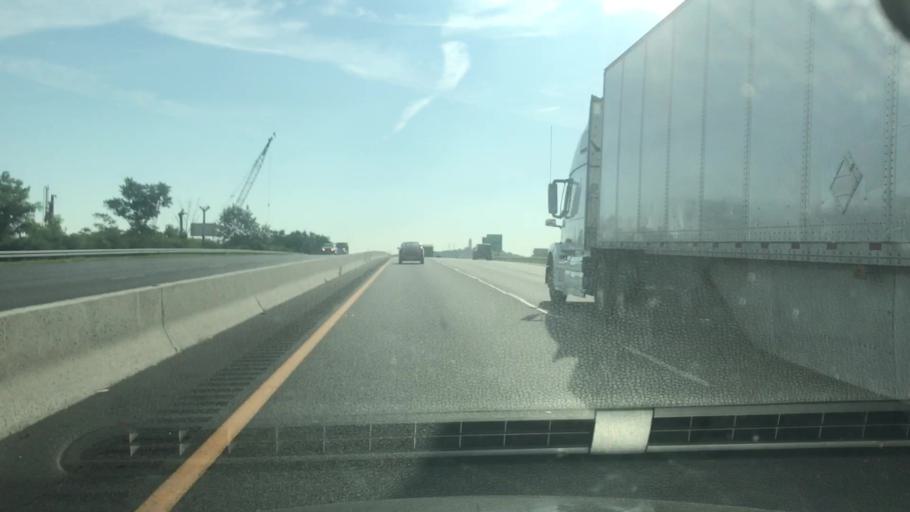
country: US
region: New Jersey
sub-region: Hudson County
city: Harrison
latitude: 40.7439
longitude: -74.1396
